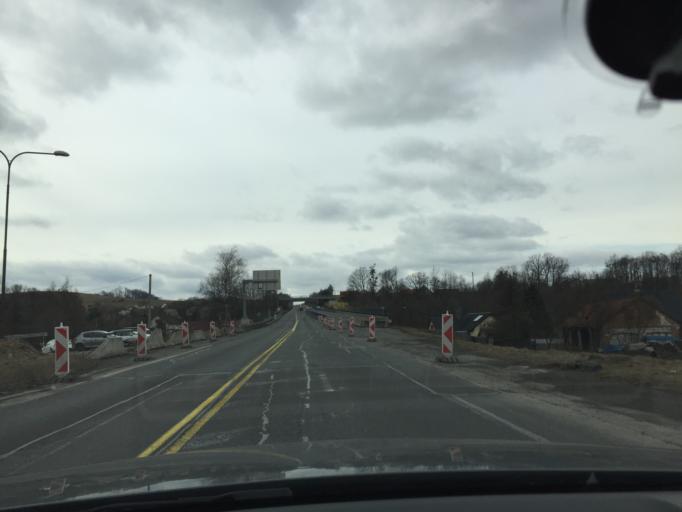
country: CZ
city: Frycovice
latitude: 49.6500
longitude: 18.2191
